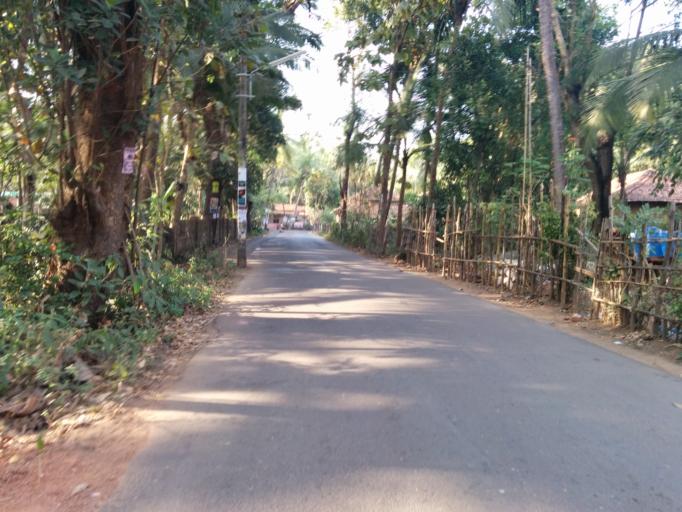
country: IN
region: Goa
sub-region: South Goa
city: Kankon
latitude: 15.0102
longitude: 74.0285
